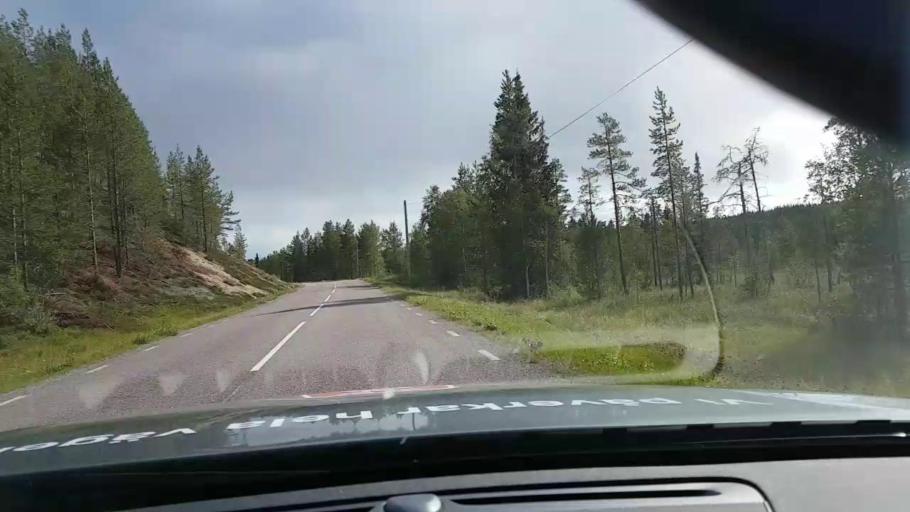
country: SE
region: Vaesterbotten
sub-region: Asele Kommun
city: Asele
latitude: 63.8689
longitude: 17.3587
